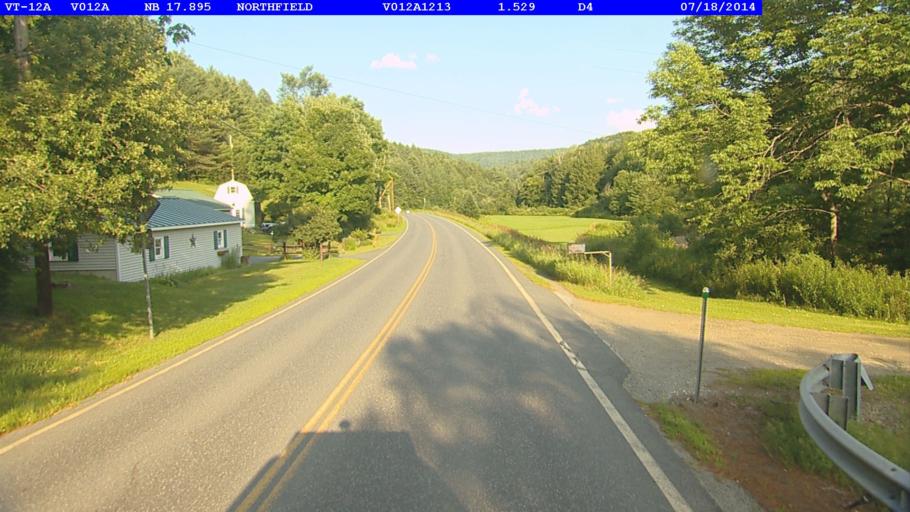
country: US
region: Vermont
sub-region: Washington County
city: Northfield
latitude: 44.1134
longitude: -72.6988
